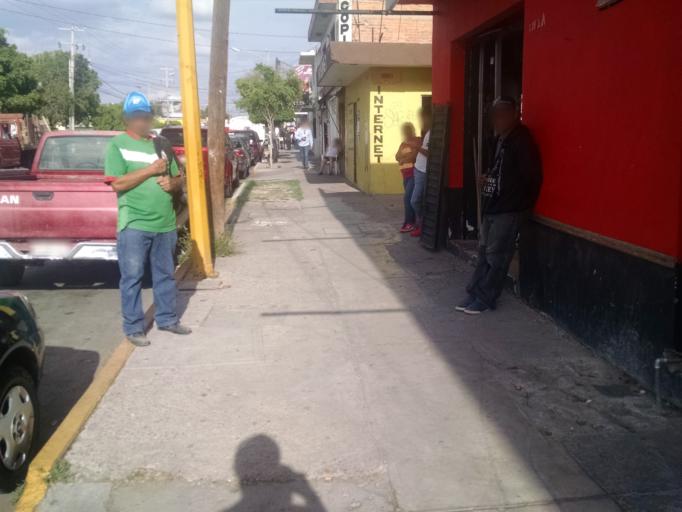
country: MX
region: Aguascalientes
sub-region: Aguascalientes
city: Aguascalientes
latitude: 21.8853
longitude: -102.3119
